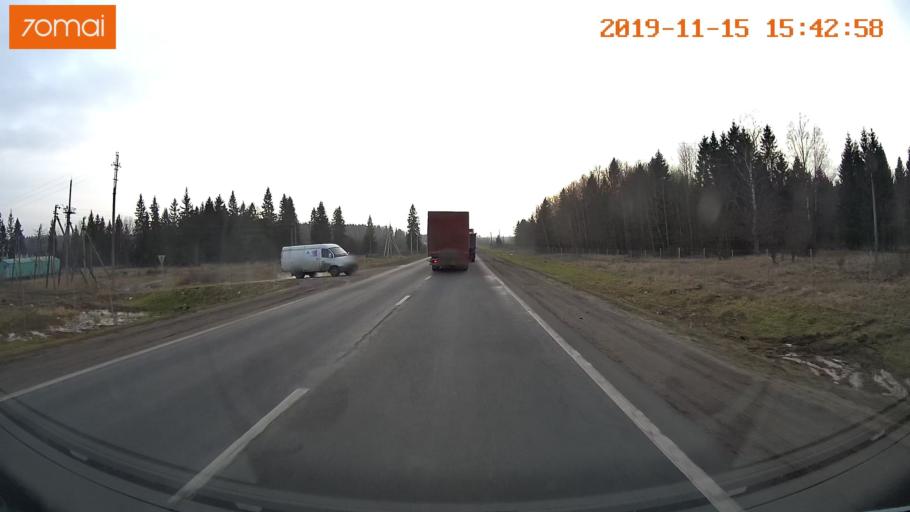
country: RU
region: Jaroslavl
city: Danilov
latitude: 57.9875
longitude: 40.0331
